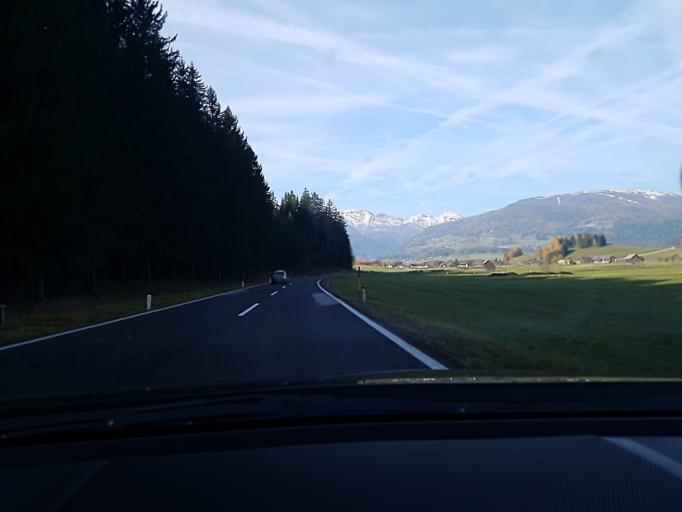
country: AT
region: Salzburg
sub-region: Politischer Bezirk Tamsweg
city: Mariapfarr
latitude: 47.1392
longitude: 13.7592
